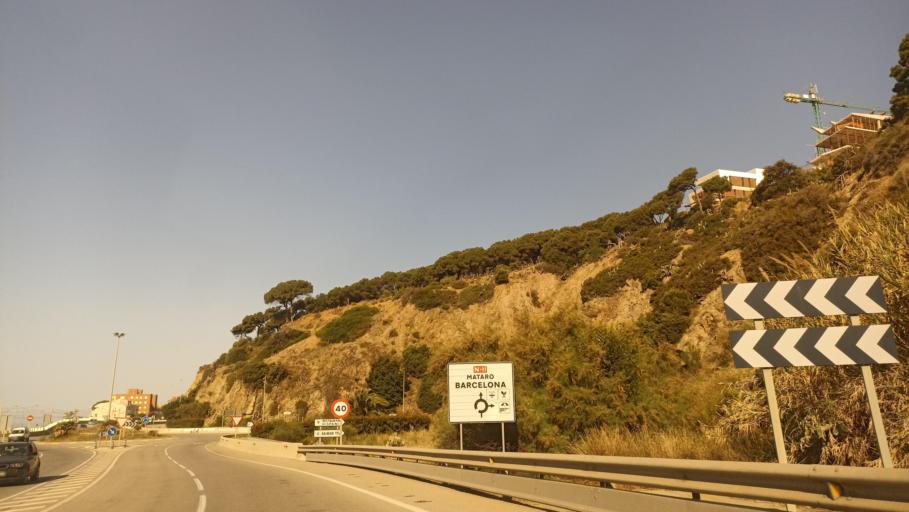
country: ES
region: Catalonia
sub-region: Provincia de Barcelona
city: Caldes d'Estrac
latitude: 41.5729
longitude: 2.5363
